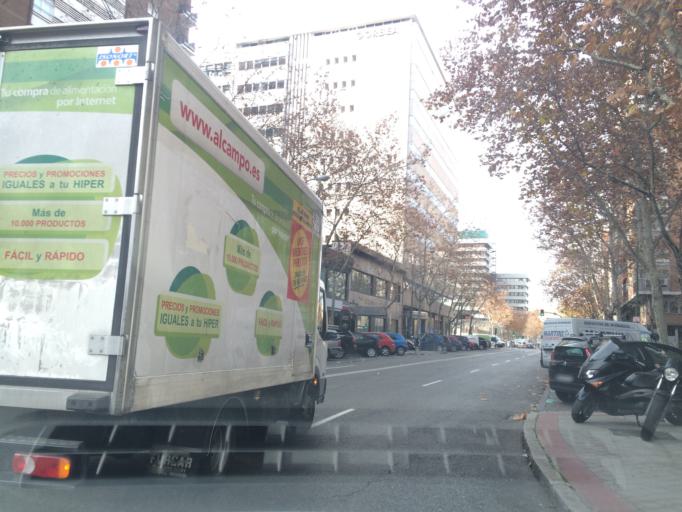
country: ES
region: Madrid
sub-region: Provincia de Madrid
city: Chamartin
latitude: 40.4621
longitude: -3.6903
